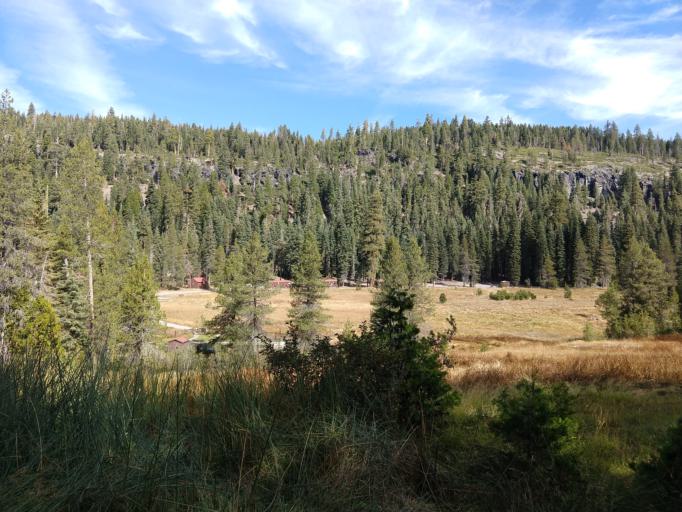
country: US
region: California
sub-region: Plumas County
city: Chester
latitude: 40.4418
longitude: -121.4033
